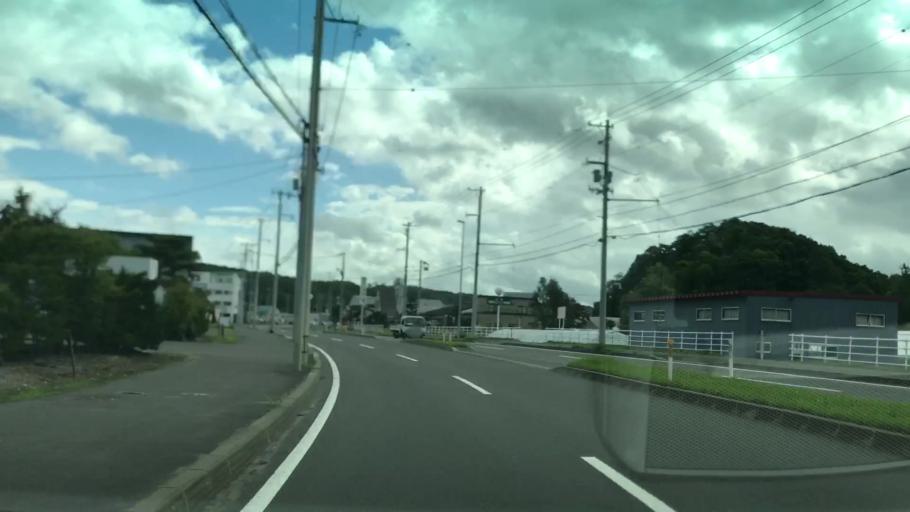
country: JP
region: Hokkaido
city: Sapporo
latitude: 42.9789
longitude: 141.4401
